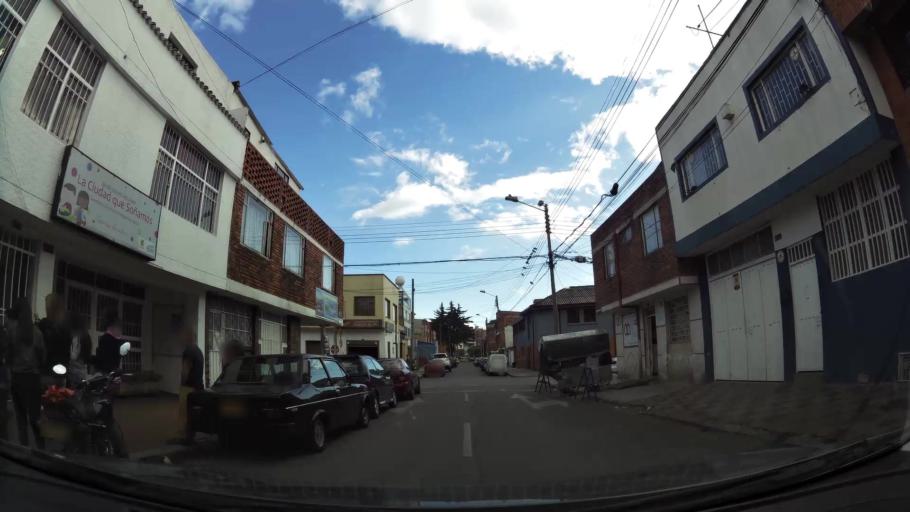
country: CO
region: Bogota D.C.
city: Bogota
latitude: 4.6545
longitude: -74.0705
